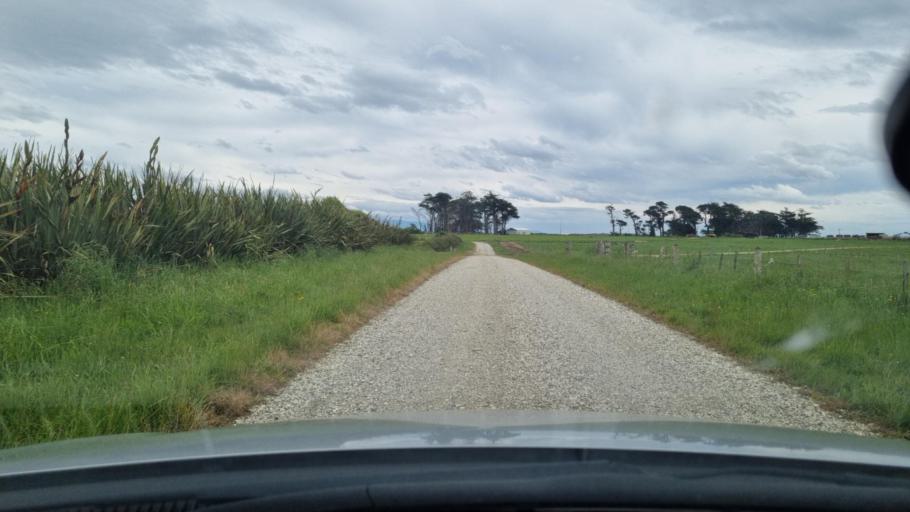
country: NZ
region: Southland
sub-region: Invercargill City
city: Invercargill
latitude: -46.4001
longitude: 168.2620
